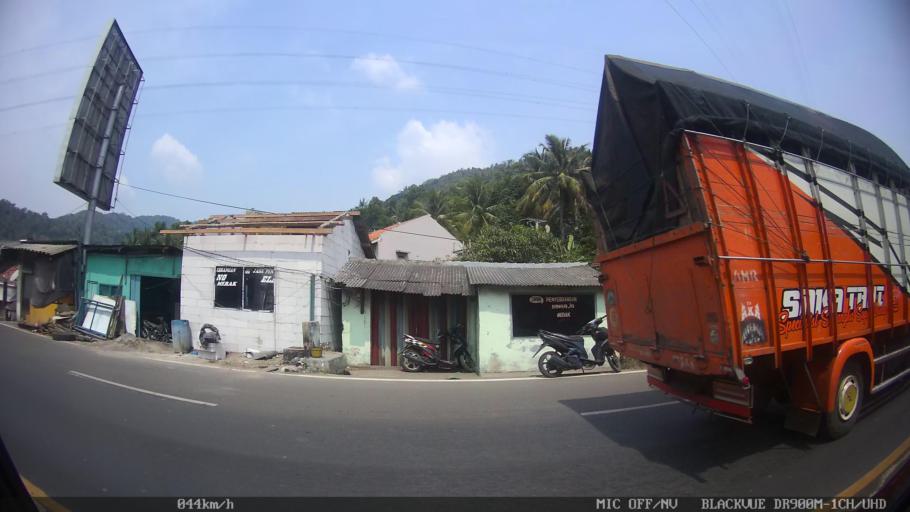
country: ID
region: Banten
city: Curug
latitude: -5.9445
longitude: 106.0047
